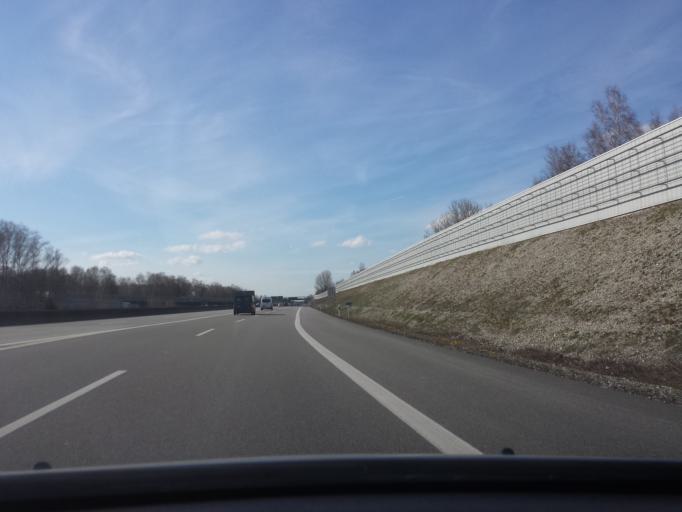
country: DE
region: Bavaria
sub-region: Upper Bavaria
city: Grobenzell
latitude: 48.2079
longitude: 11.3921
